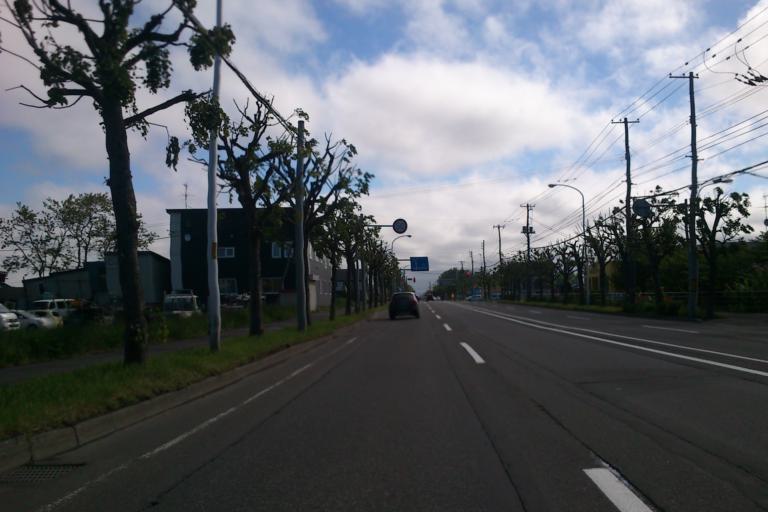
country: JP
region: Hokkaido
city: Sapporo
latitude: 43.1358
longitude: 141.2667
